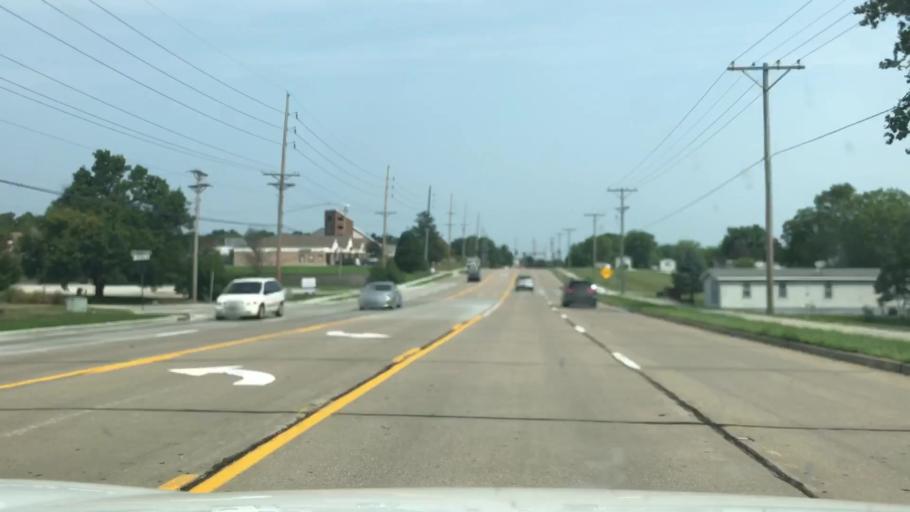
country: US
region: Missouri
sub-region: Saint Charles County
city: Dardenne Prairie
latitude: 38.7896
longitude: -90.7367
